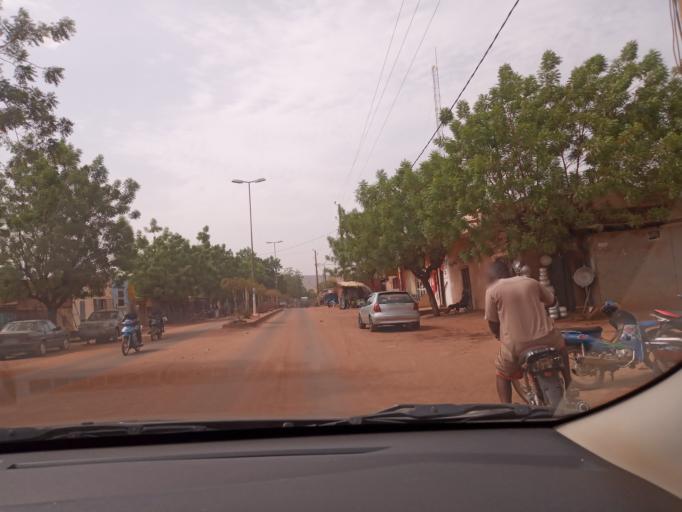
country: ML
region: Bamako
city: Bamako
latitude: 12.6758
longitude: -7.9243
